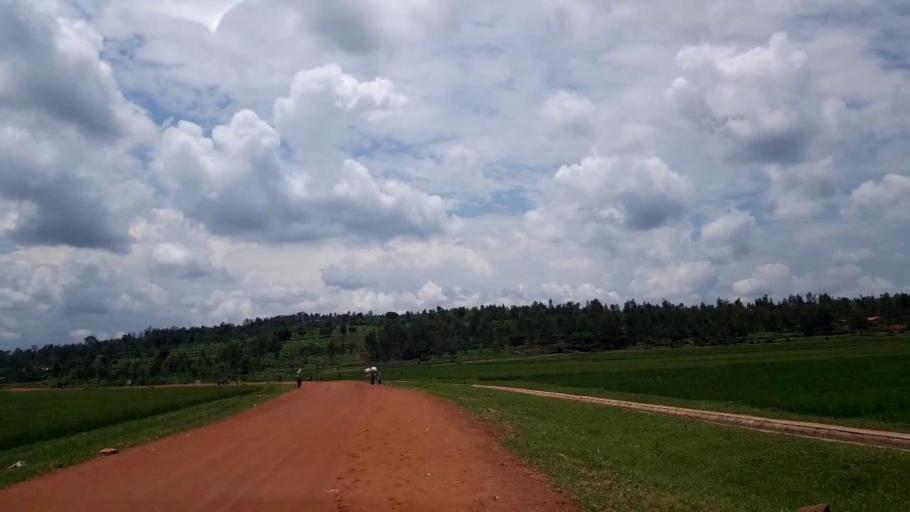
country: RW
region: Northern Province
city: Byumba
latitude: -1.5701
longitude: 30.2918
